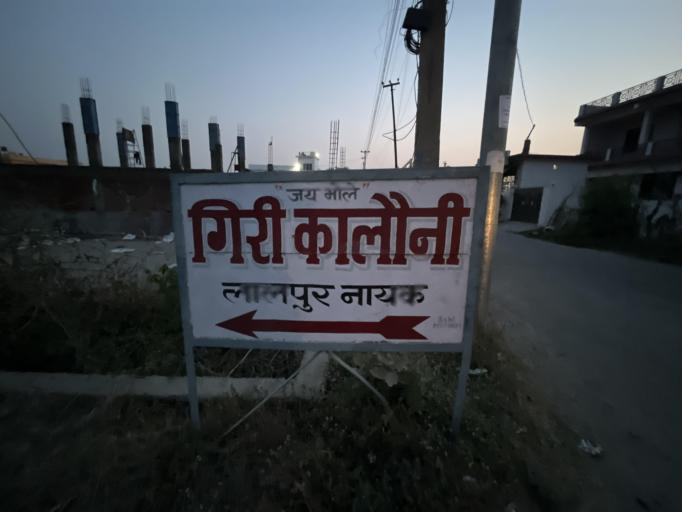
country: IN
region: Uttarakhand
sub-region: Naini Tal
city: Haldwani
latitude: 29.2012
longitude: 79.4779
